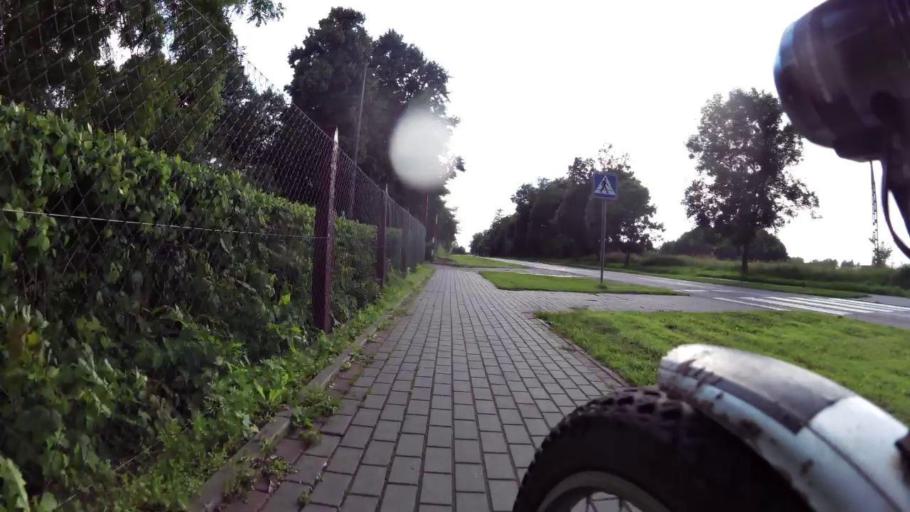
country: PL
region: West Pomeranian Voivodeship
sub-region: Powiat swidwinski
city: Swidwin
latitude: 53.7769
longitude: 15.8569
